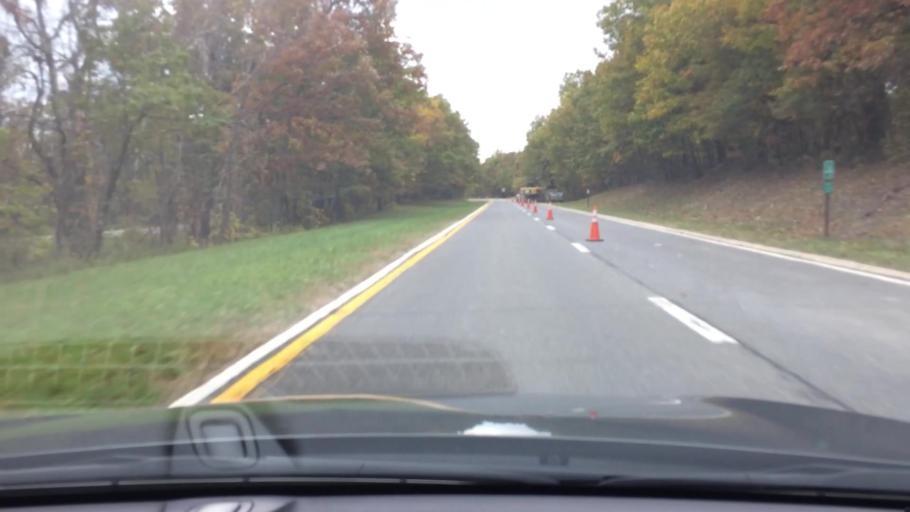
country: US
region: New York
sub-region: Dutchess County
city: Pine Plains
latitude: 42.0937
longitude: -73.7211
